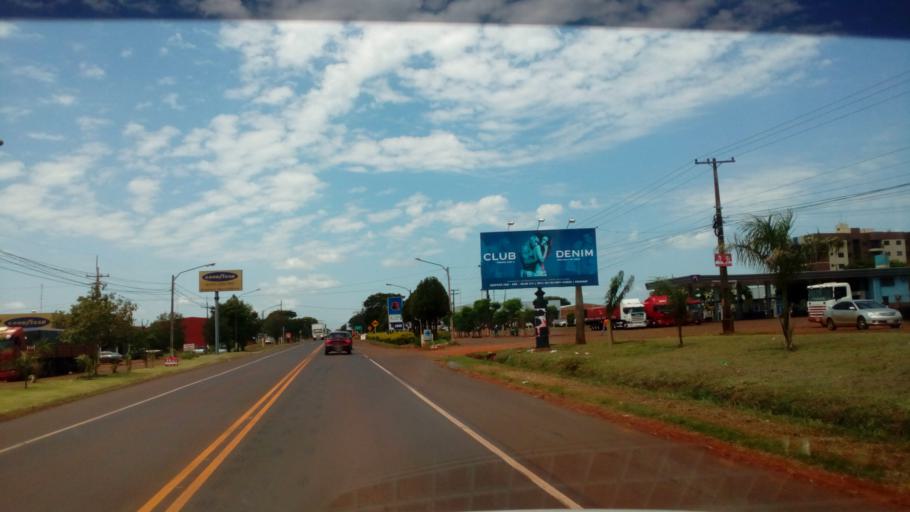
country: PY
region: Alto Parana
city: Santa Rita
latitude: -25.7732
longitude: -55.0724
